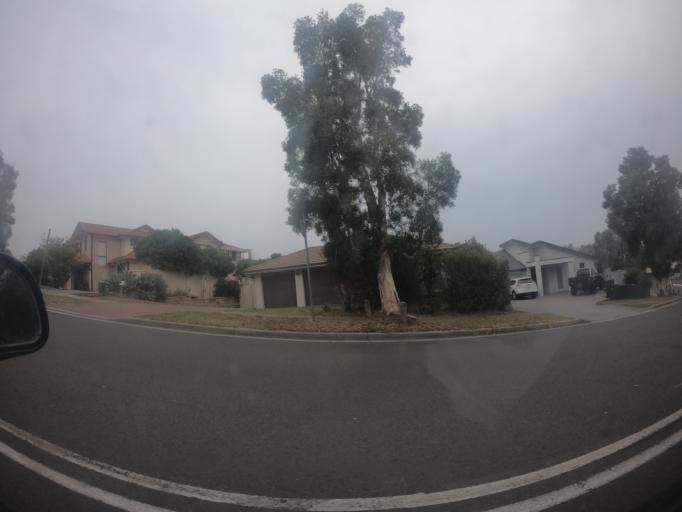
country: AU
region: New South Wales
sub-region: Shellharbour
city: Flinders
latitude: -34.5825
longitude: 150.8472
